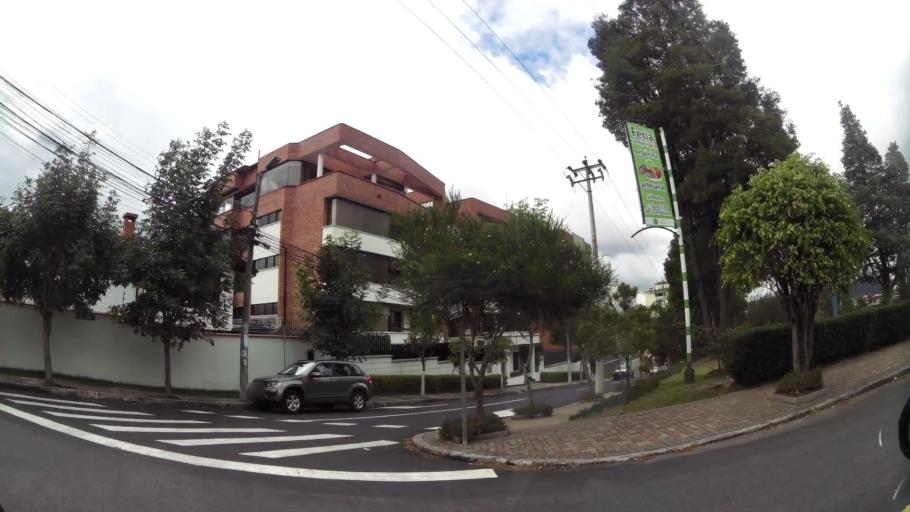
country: EC
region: Pichincha
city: Quito
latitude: -0.1656
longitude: -78.4930
